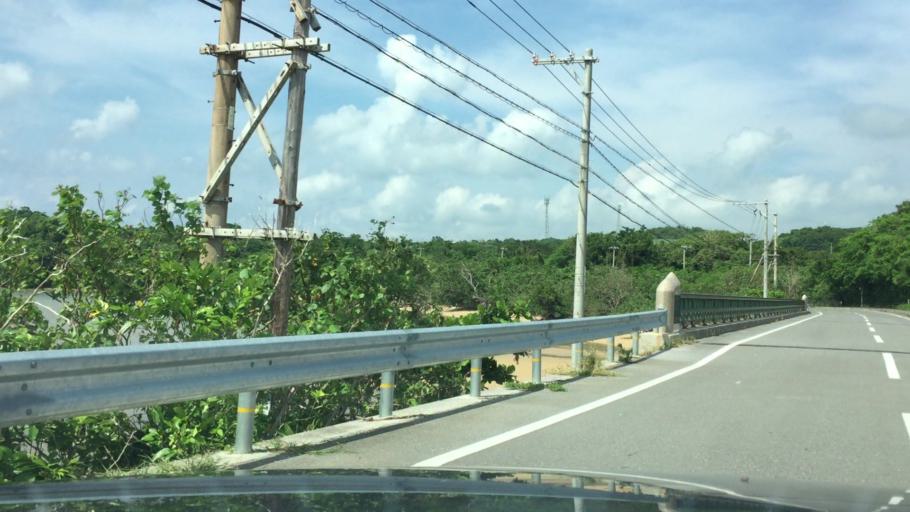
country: JP
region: Okinawa
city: Ishigaki
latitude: 24.4871
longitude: 124.2299
